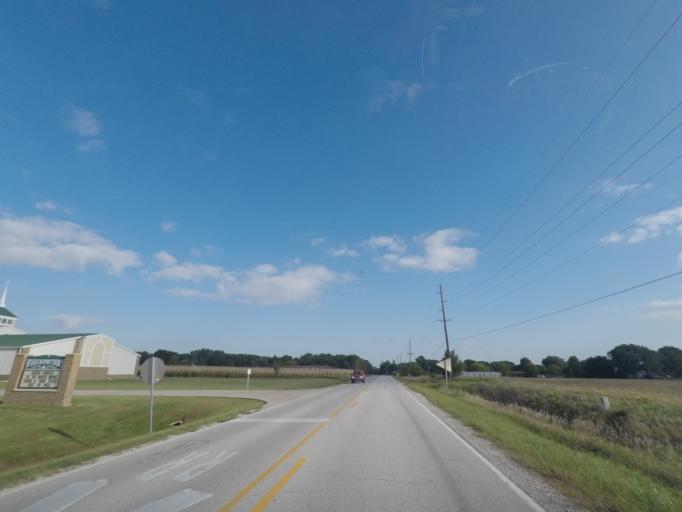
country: US
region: Iowa
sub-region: Story County
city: Nevada
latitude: 42.0127
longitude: -93.4628
